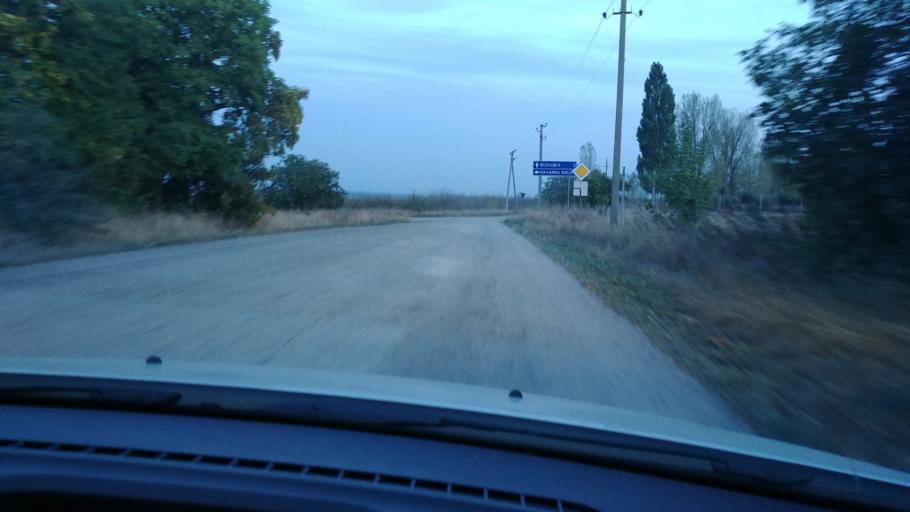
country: MD
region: Rezina
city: Saharna
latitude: 47.6693
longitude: 28.9440
